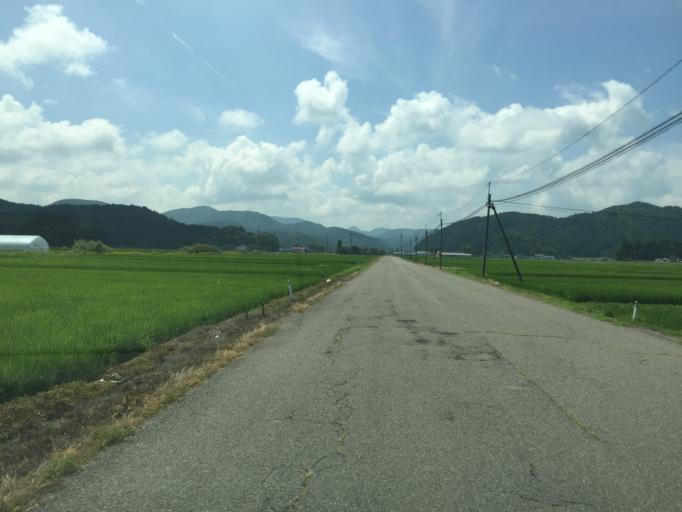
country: JP
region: Fukushima
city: Inawashiro
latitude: 37.4039
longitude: 140.0856
